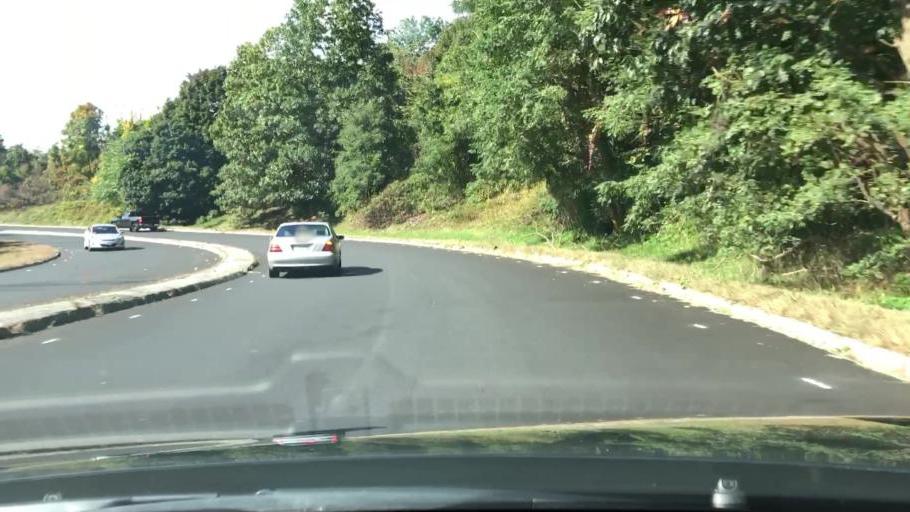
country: US
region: Massachusetts
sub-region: Essex County
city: Methuen
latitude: 42.7340
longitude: -71.1897
